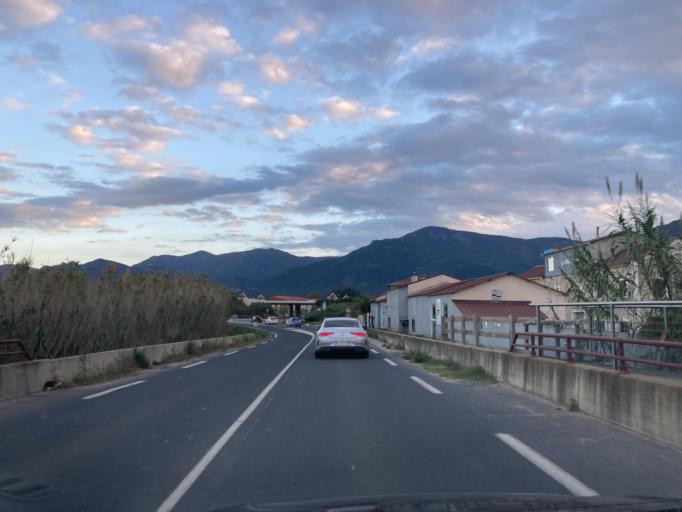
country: FR
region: Languedoc-Roussillon
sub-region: Departement des Pyrenees-Orientales
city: Sant Genis de Fontanes
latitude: 42.5501
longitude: 2.9171
